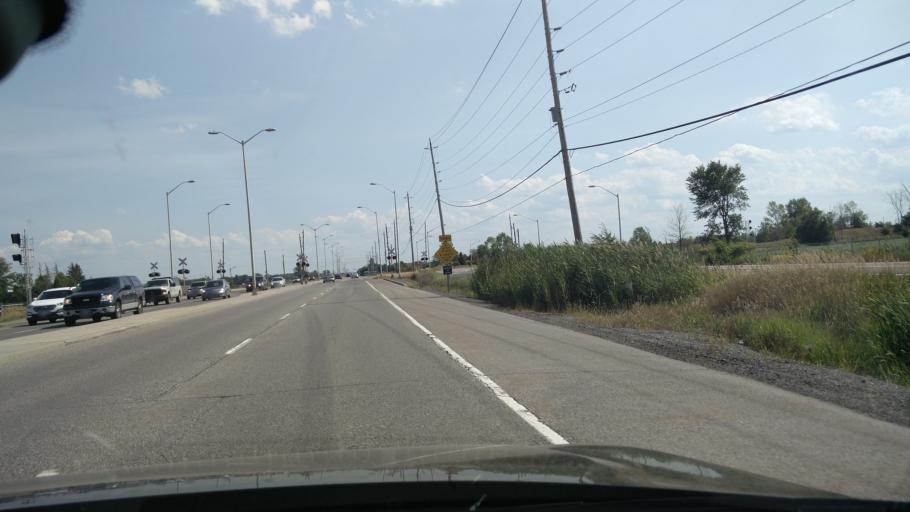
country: CA
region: Ontario
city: Bells Corners
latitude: 45.3041
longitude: -75.7345
